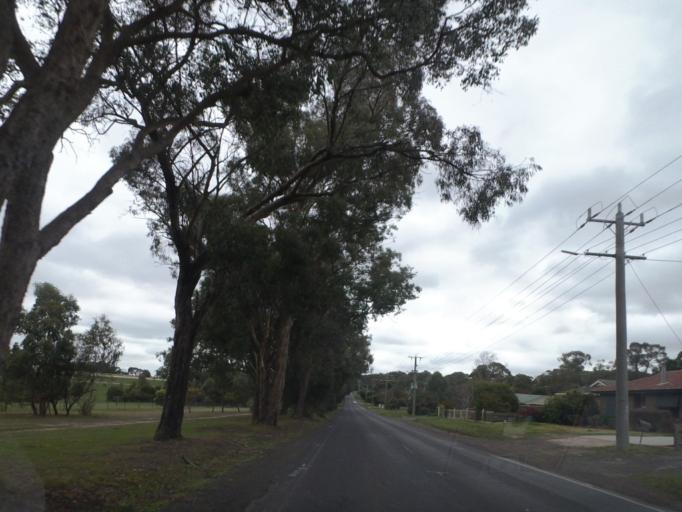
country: AU
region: Victoria
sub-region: Nillumbik
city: Doreen
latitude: -37.6249
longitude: 145.1348
